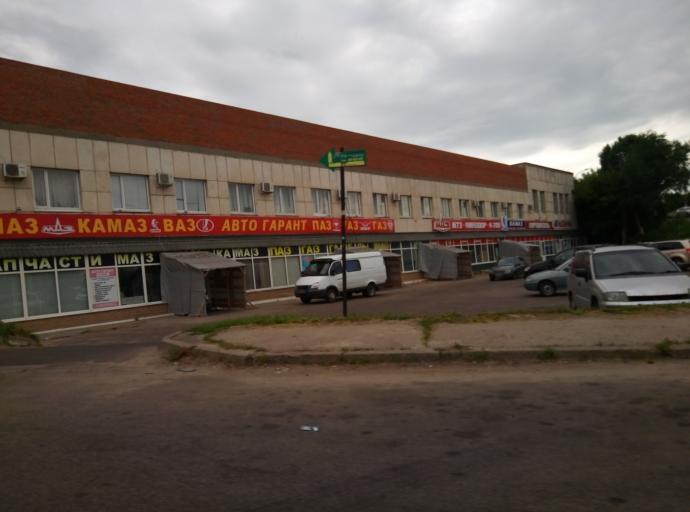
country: RU
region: Kursk
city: Kursk
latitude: 51.7073
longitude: 36.1650
